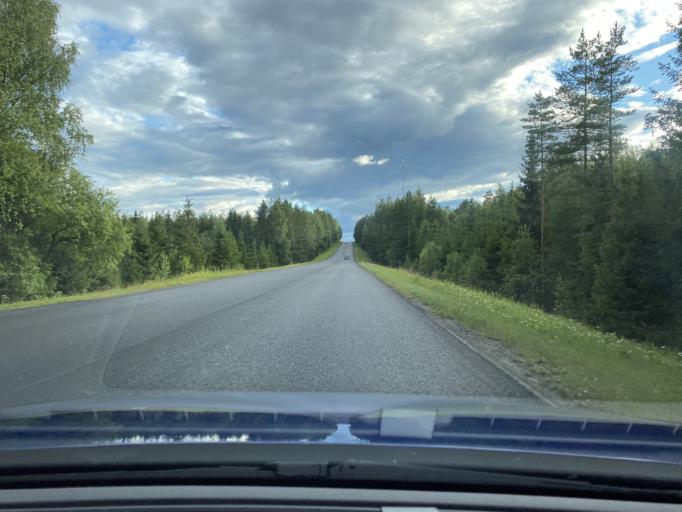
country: FI
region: Haeme
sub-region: Haemeenlinna
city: Haemeenlinna
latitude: 60.9398
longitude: 24.3820
